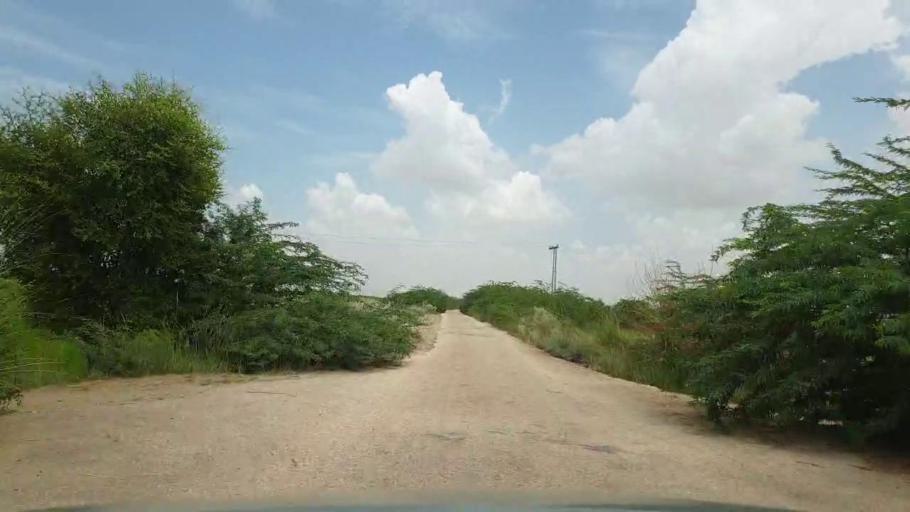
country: PK
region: Sindh
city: Bozdar
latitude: 27.0244
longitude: 68.9505
